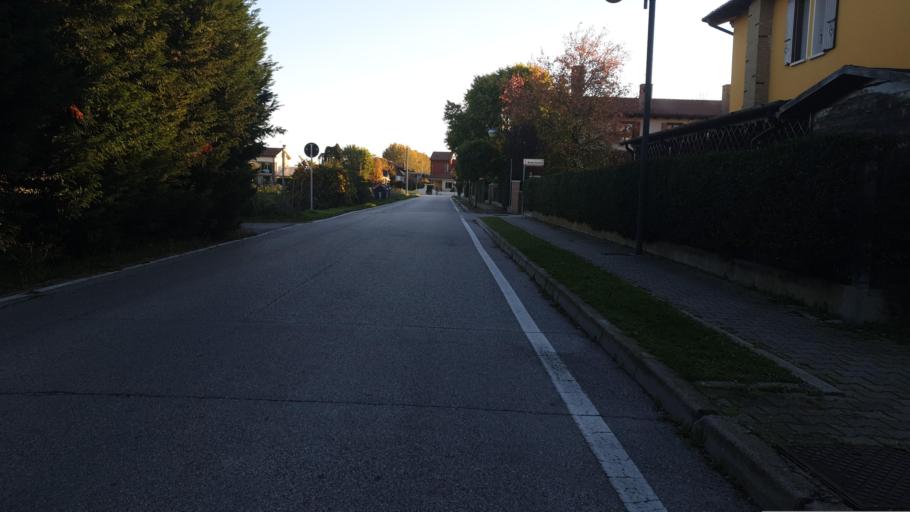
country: IT
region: Veneto
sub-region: Provincia di Venezia
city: Marano
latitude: 45.4560
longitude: 12.1025
